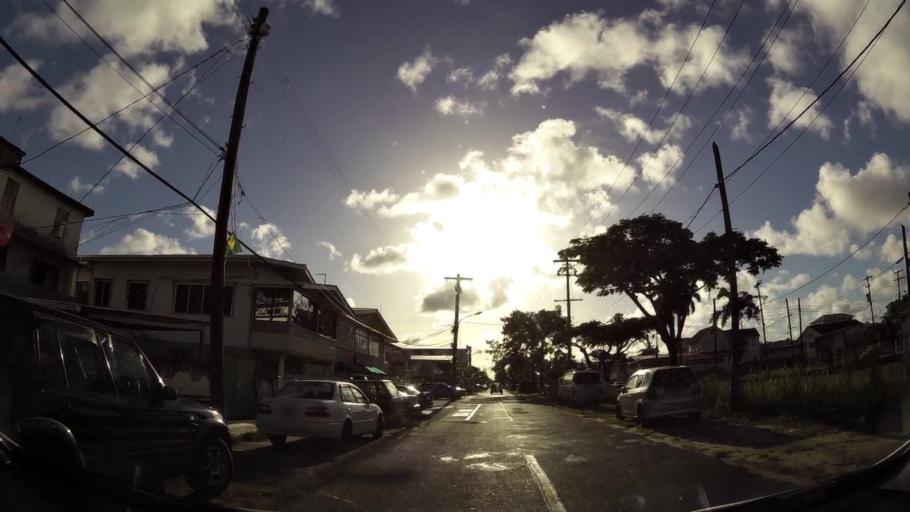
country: GY
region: Demerara-Mahaica
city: Georgetown
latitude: 6.8069
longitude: -58.1554
